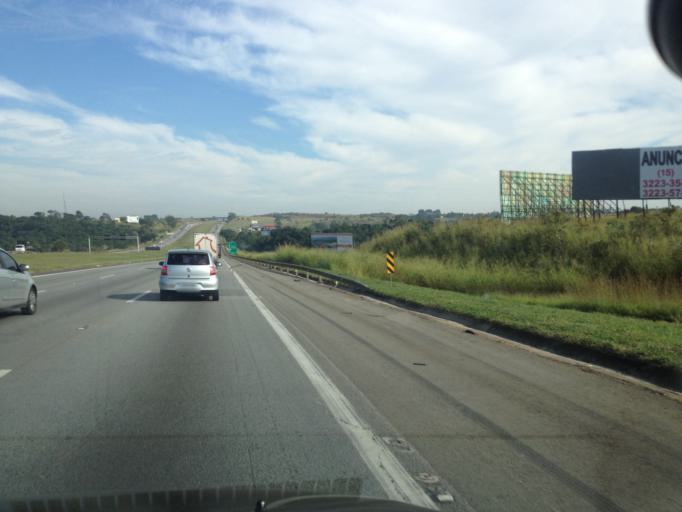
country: BR
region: Sao Paulo
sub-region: Itu
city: Itu
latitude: -23.4034
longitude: -47.3186
